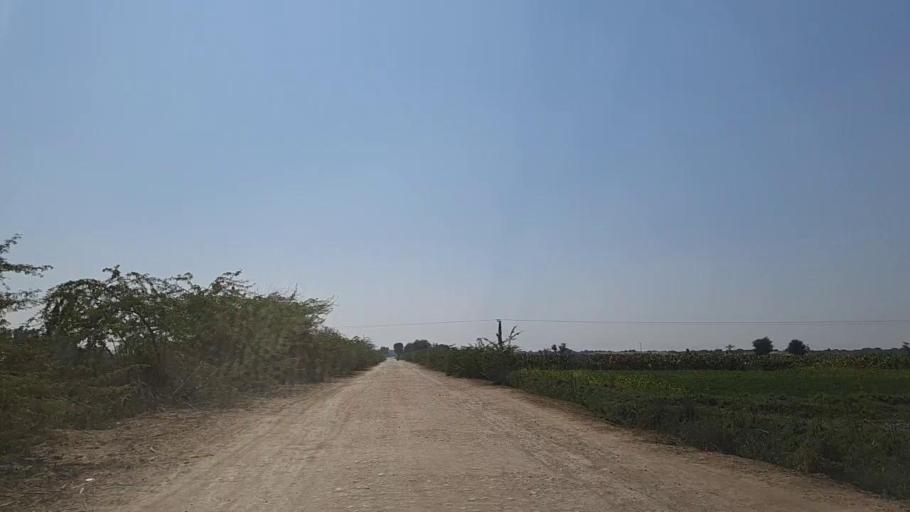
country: PK
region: Sindh
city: Samaro
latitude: 25.3526
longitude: 69.3148
